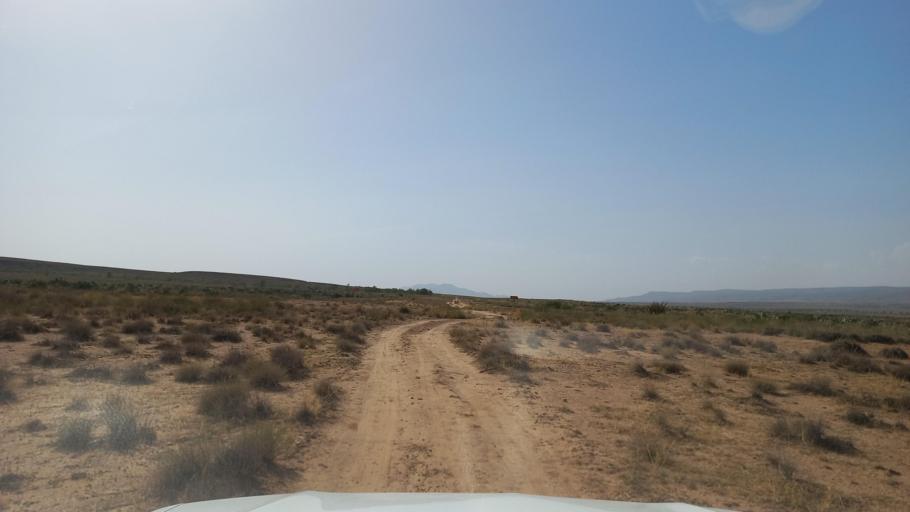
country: TN
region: Al Qasrayn
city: Kasserine
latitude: 35.2142
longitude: 9.0047
